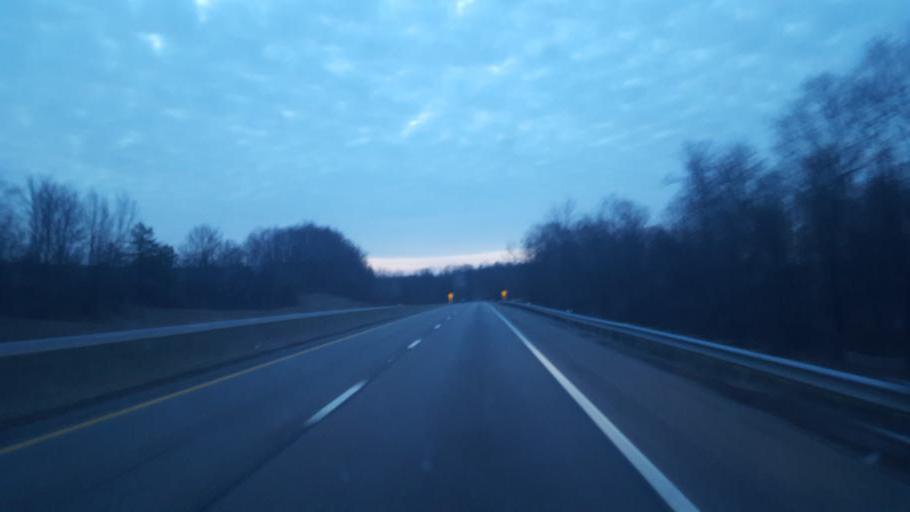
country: US
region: Ohio
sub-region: Jackson County
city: Oak Hill
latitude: 38.9796
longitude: -82.5249
